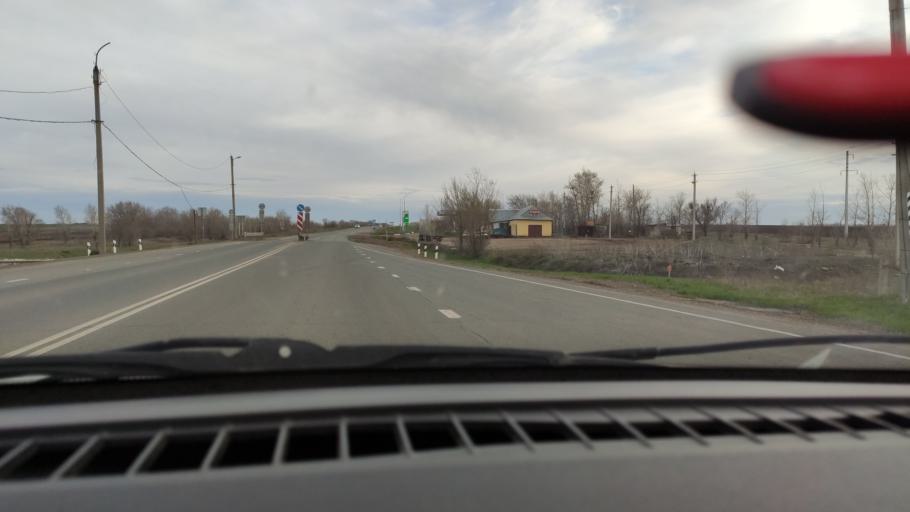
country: RU
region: Orenburg
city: Sakmara
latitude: 52.1699
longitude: 55.2908
